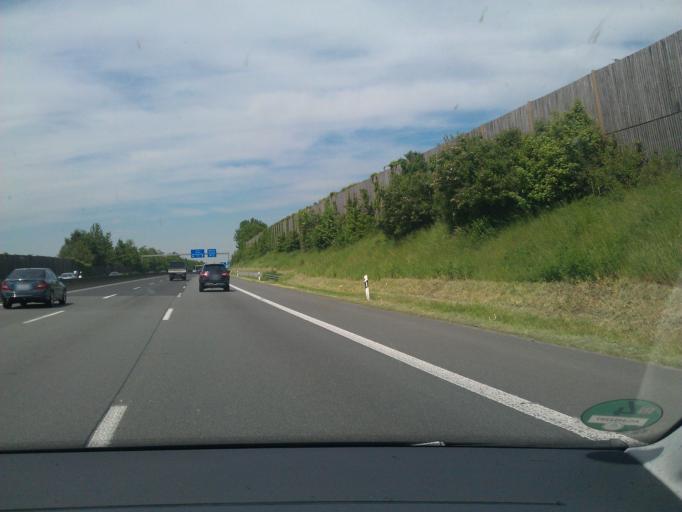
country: DE
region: North Rhine-Westphalia
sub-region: Regierungsbezirk Koln
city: Titz
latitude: 51.0795
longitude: 6.4245
